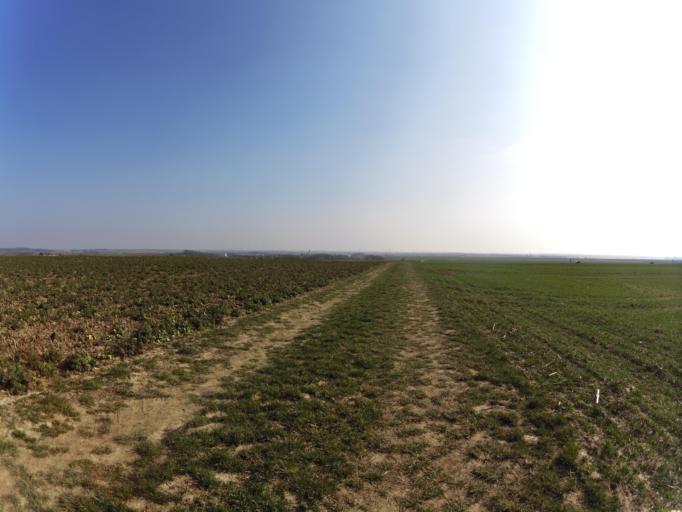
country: DE
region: Bavaria
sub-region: Regierungsbezirk Unterfranken
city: Gaukonigshofen
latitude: 49.6491
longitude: 9.9866
